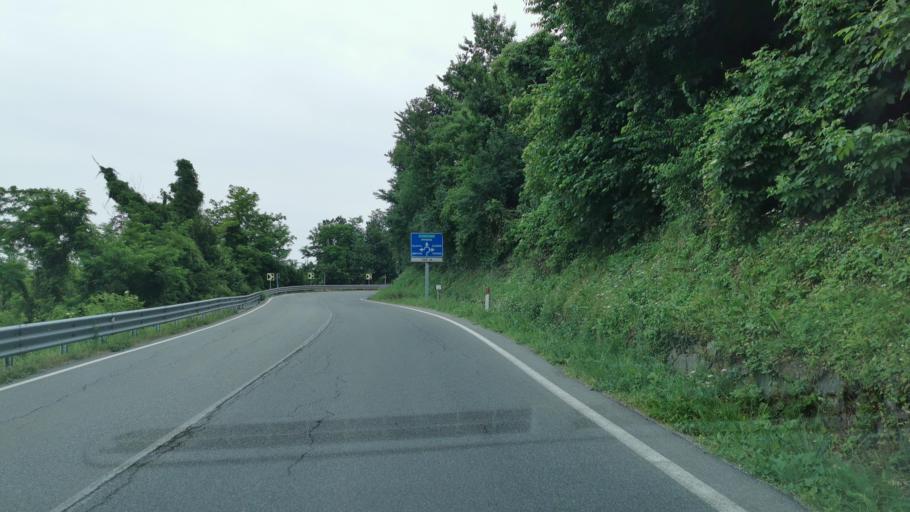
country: IT
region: Piedmont
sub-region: Provincia di Cuneo
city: Ceva
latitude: 44.3803
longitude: 8.0402
